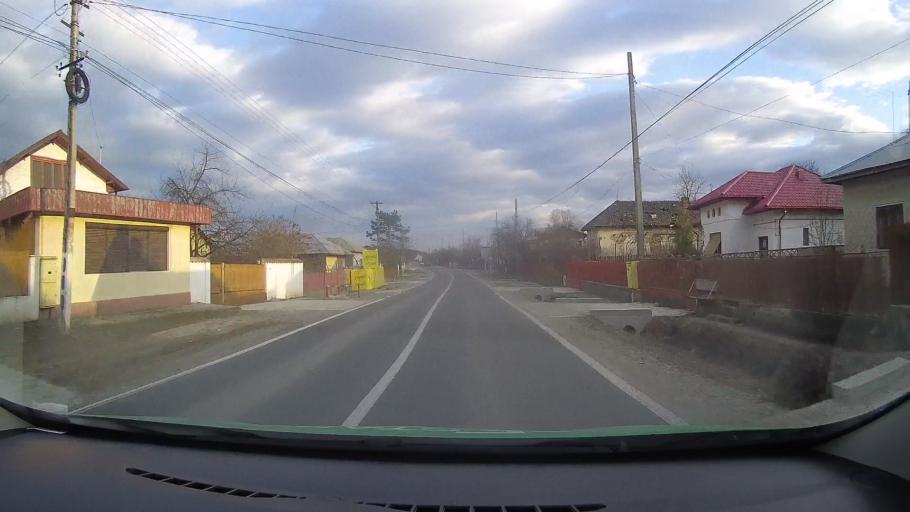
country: RO
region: Dambovita
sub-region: Comuna I. L. Caragiale
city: Ghirdoveni
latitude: 44.9388
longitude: 25.6798
